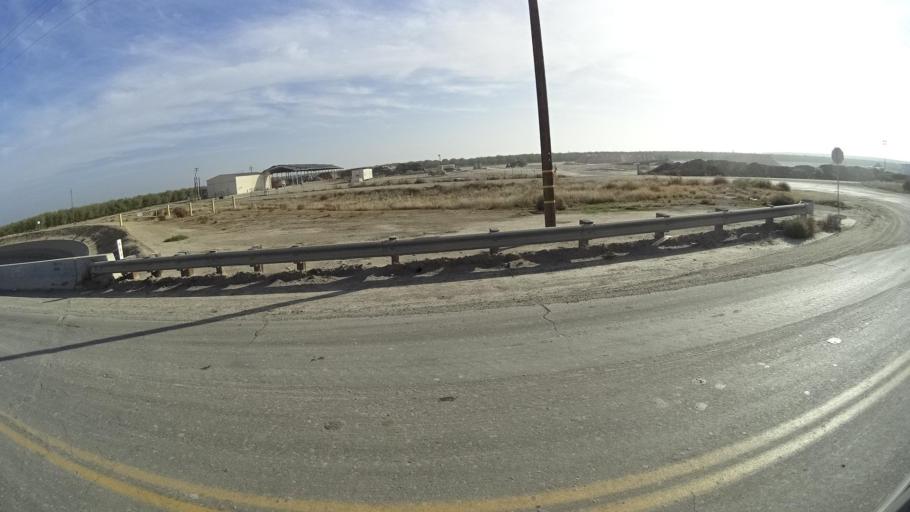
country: US
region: California
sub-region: Kern County
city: McFarland
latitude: 35.6447
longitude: -119.2045
